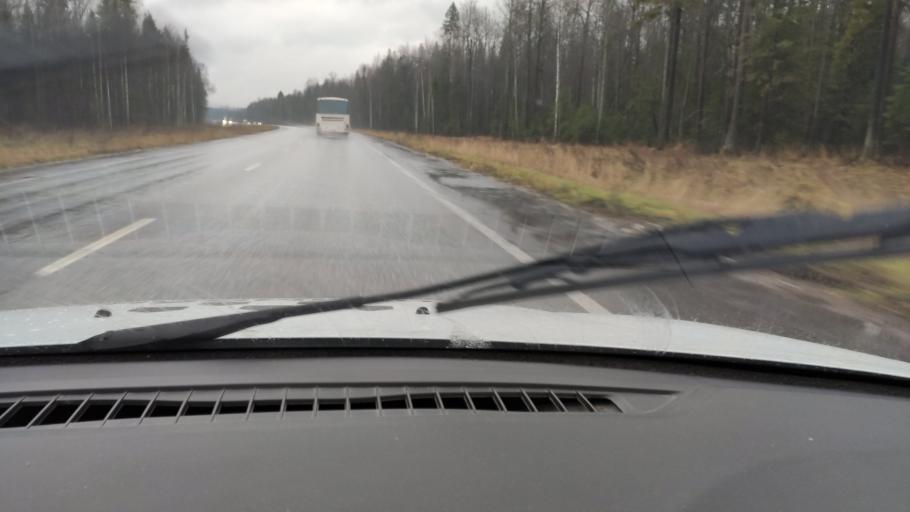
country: RU
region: Perm
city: Novyye Lyady
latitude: 58.0347
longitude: 56.5327
